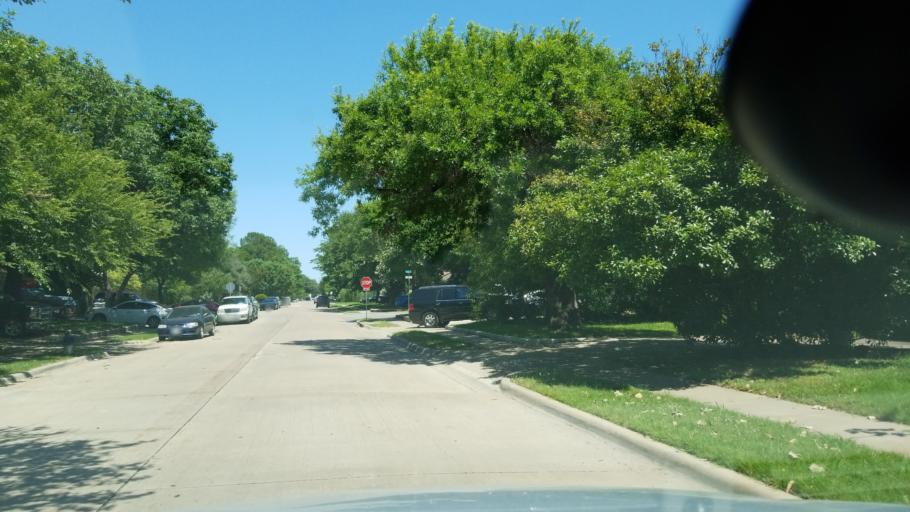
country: US
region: Texas
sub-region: Dallas County
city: Irving
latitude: 32.8351
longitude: -96.9340
